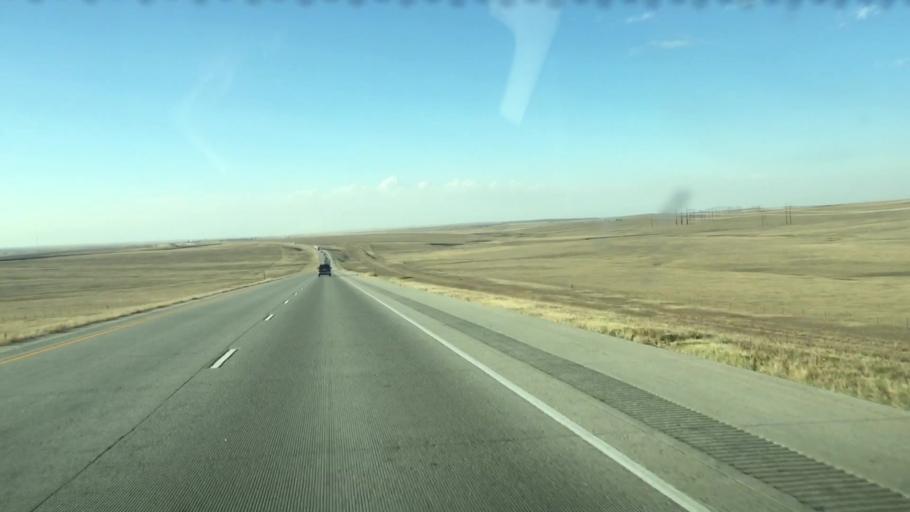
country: US
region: Colorado
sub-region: Lincoln County
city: Limon
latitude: 39.4042
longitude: -103.8958
